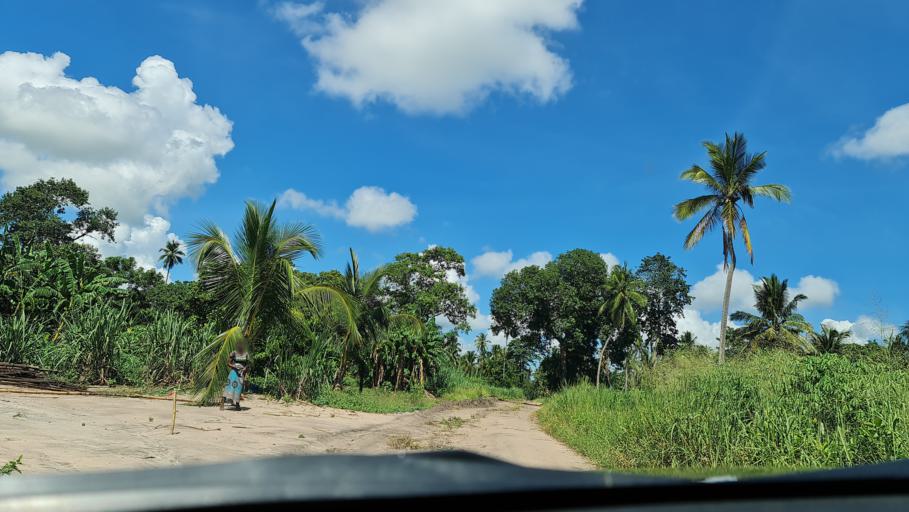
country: MZ
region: Zambezia
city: Quelimane
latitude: -17.3841
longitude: 37.5299
